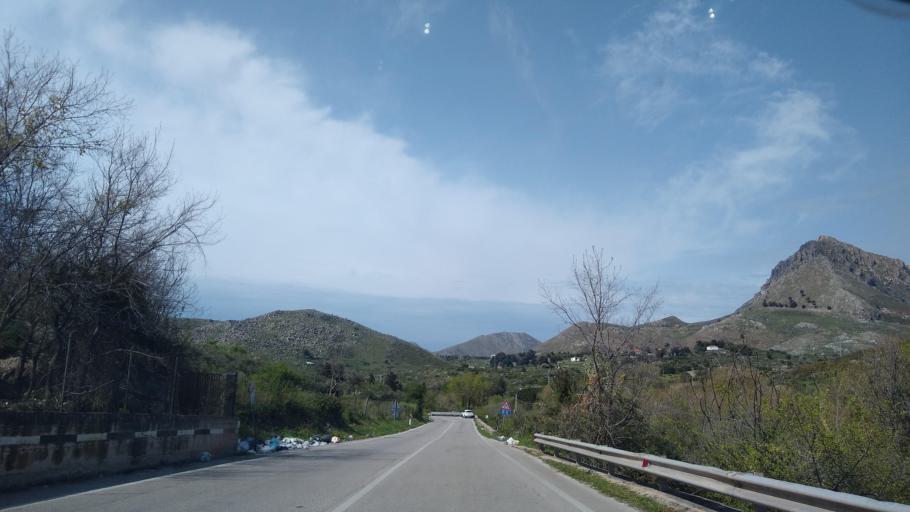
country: IT
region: Sicily
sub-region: Palermo
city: Pioppo
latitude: 38.0419
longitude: 13.1995
